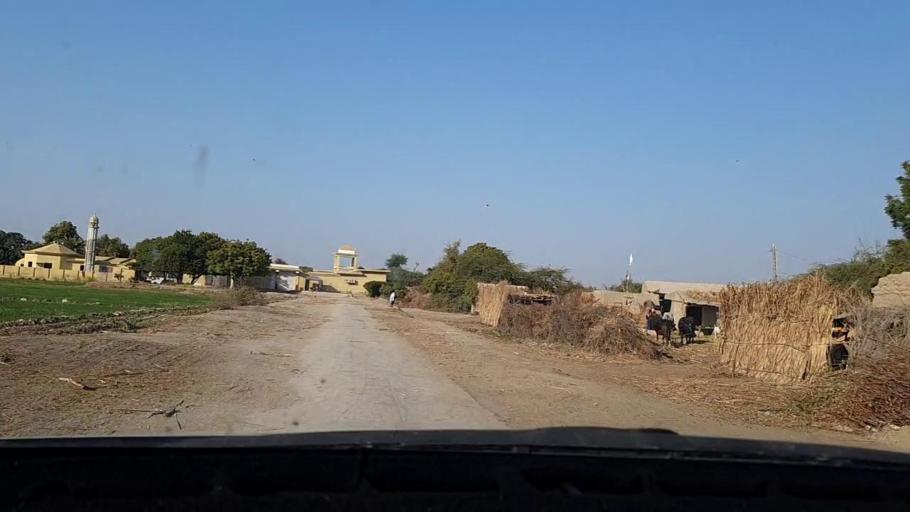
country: PK
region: Sindh
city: Tando Mittha Khan
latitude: 25.8569
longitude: 69.3334
